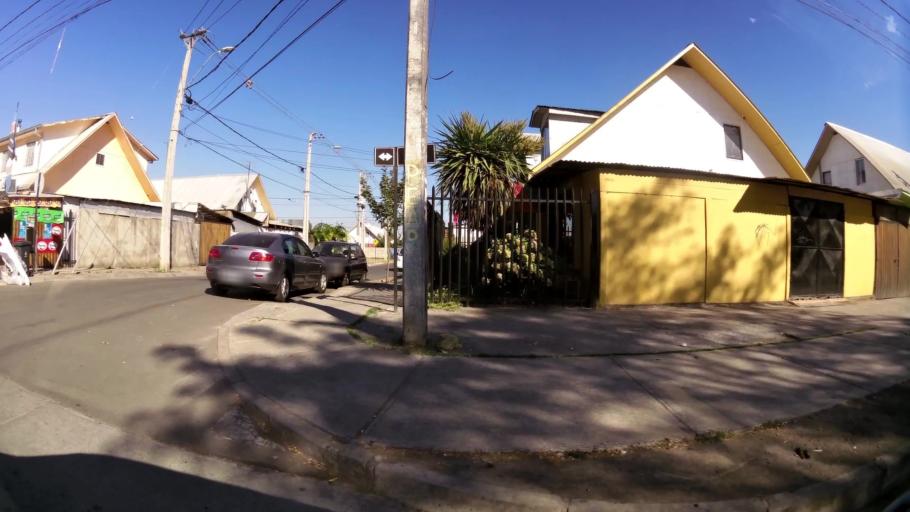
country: CL
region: Maule
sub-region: Provincia de Curico
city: Curico
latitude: -34.9935
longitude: -71.2555
